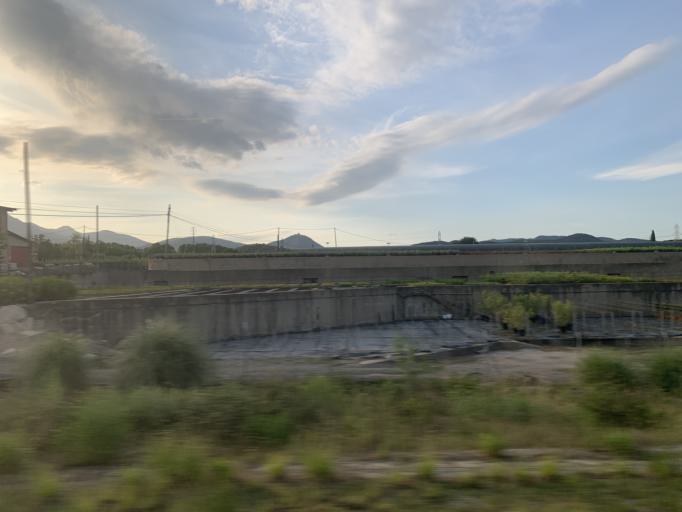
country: ES
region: Catalonia
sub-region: Provincia de Girona
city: Breda
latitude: 41.7278
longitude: 2.5726
